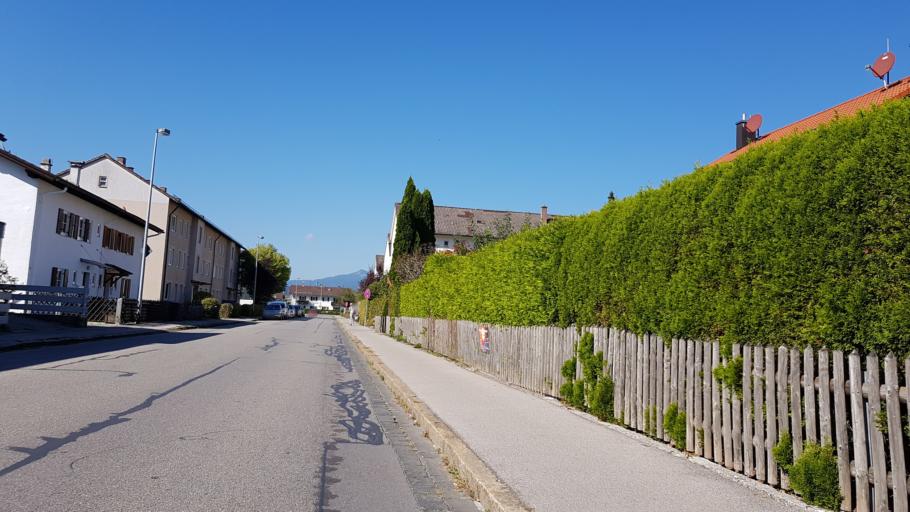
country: DE
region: Bavaria
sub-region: Swabia
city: Fuessen
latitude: 47.5732
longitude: 10.6805
